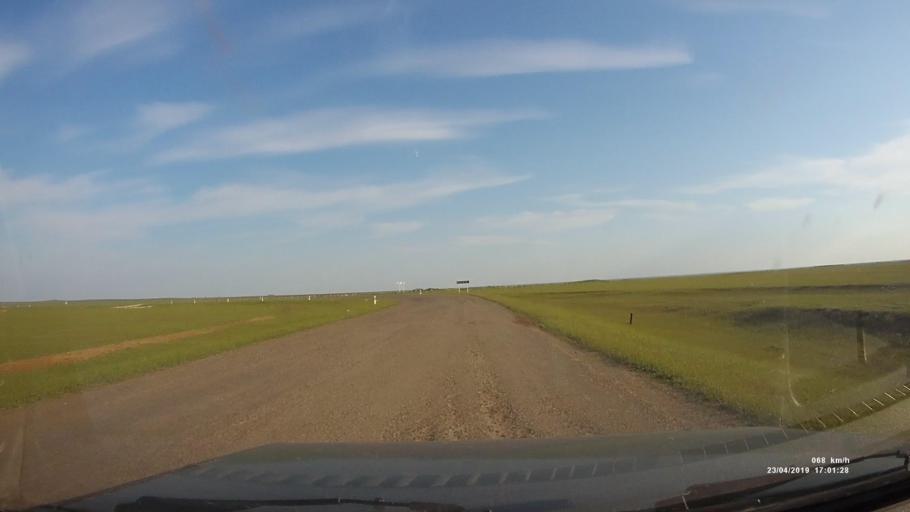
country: RU
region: Kalmykiya
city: Priyutnoye
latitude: 46.2957
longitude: 43.4081
